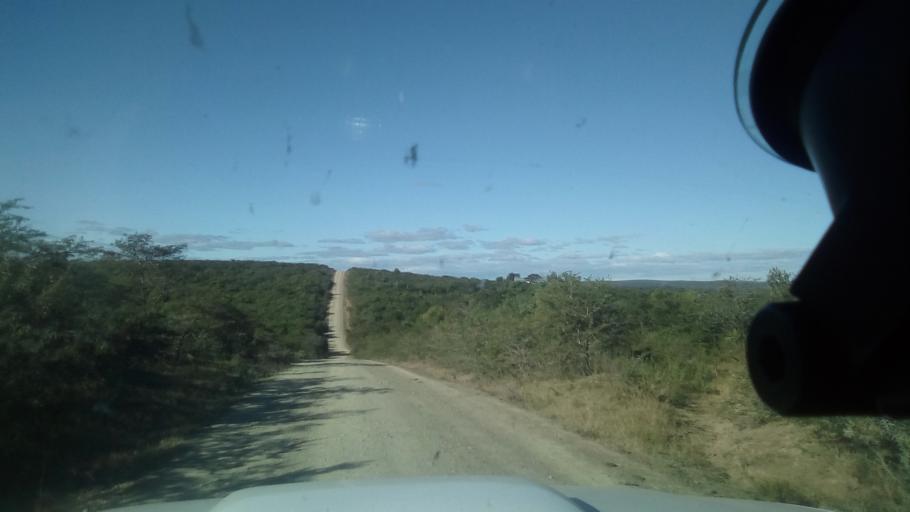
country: ZA
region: Eastern Cape
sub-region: Buffalo City Metropolitan Municipality
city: Bhisho
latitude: -32.7526
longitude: 27.3461
